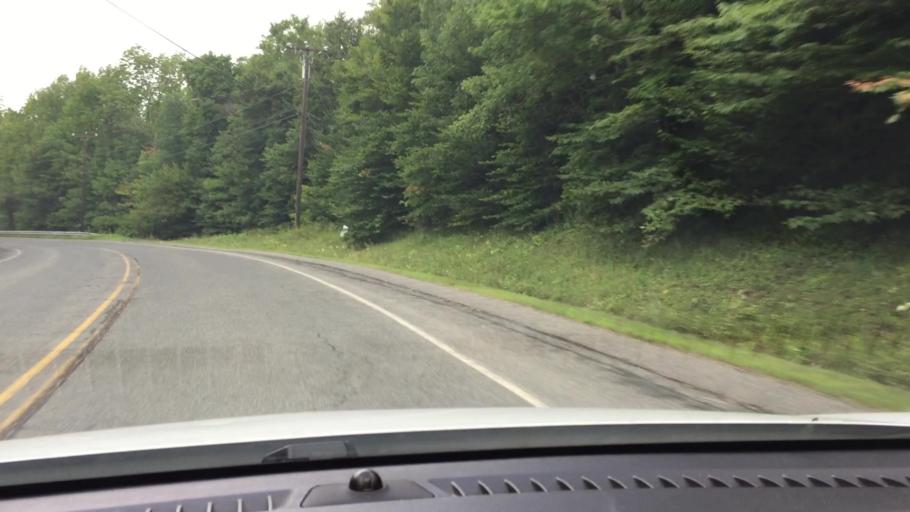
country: US
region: Massachusetts
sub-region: Berkshire County
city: Hinsdale
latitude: 42.4451
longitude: -73.0555
